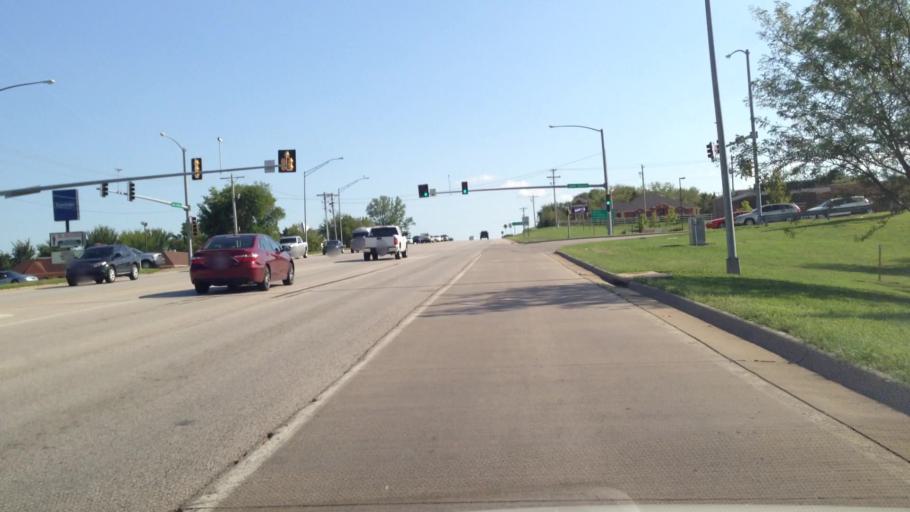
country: US
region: Kansas
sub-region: Bourbon County
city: Fort Scott
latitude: 37.8091
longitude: -94.7055
